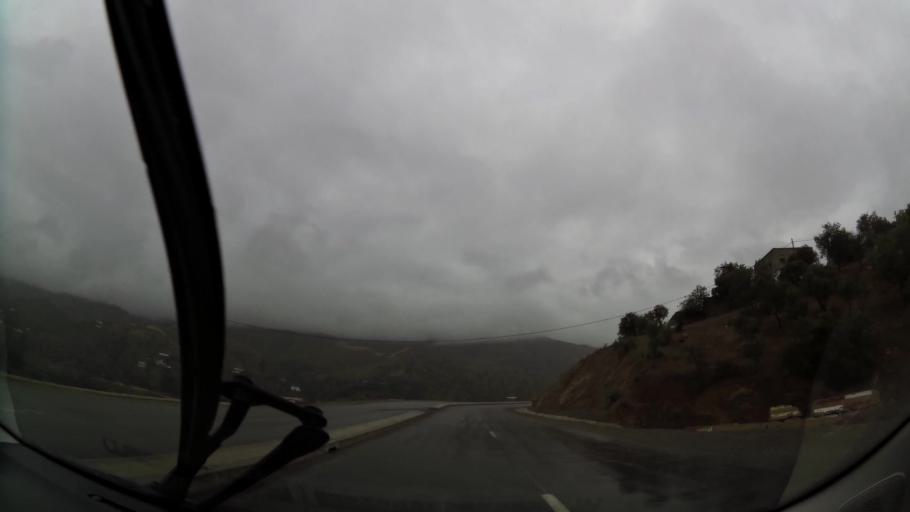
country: MA
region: Taza-Al Hoceima-Taounate
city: Imzourene
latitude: 35.0319
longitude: -3.8224
